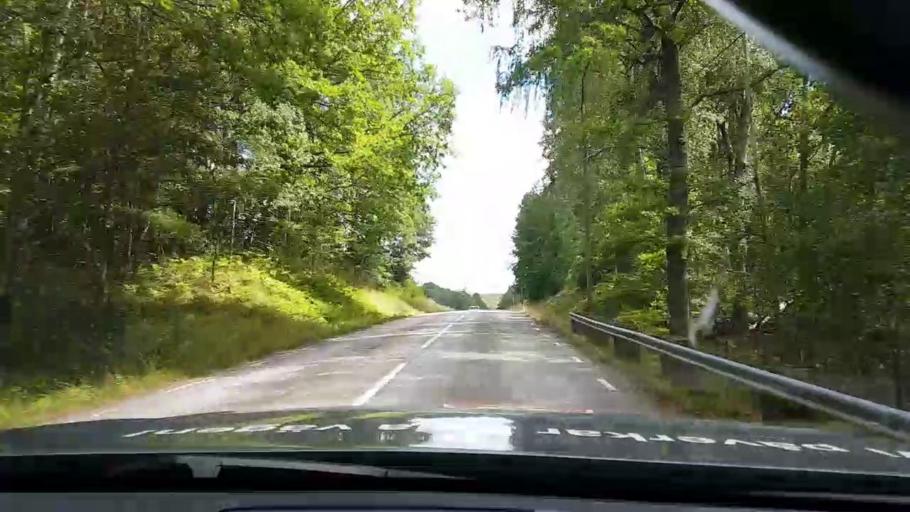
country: SE
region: Kalmar
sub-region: Vasterviks Kommun
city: Forserum
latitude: 58.0384
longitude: 16.4391
